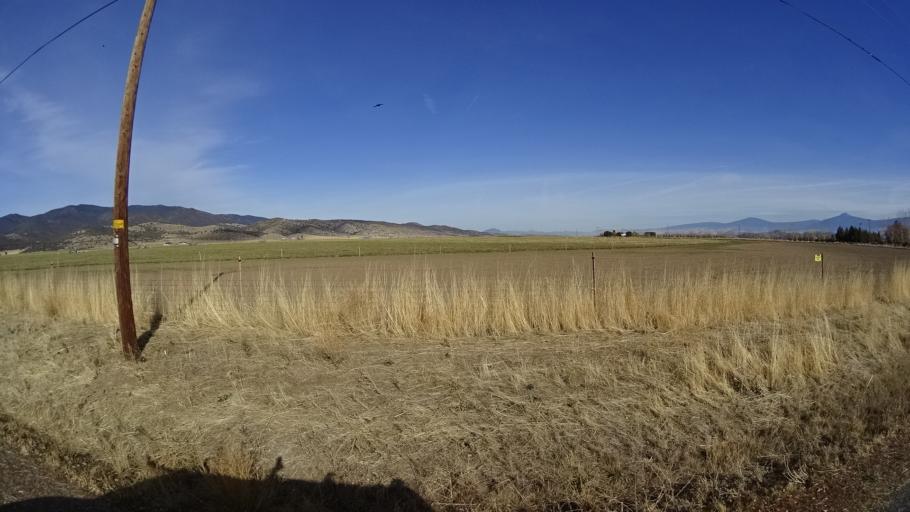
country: US
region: California
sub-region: Siskiyou County
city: Montague
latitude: 41.5381
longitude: -122.5563
